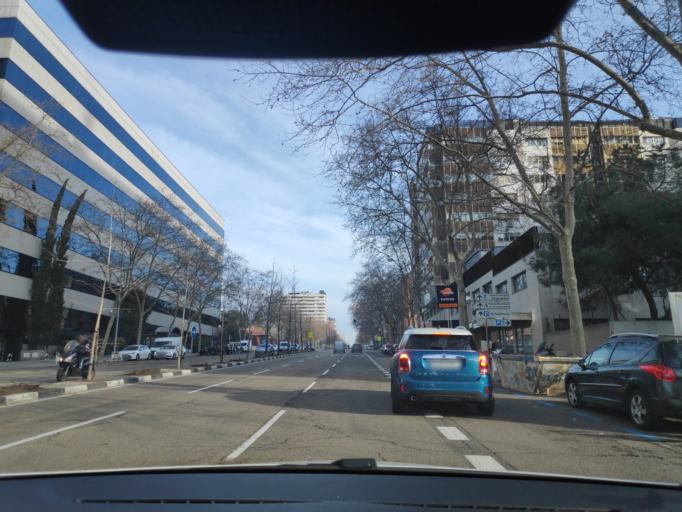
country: ES
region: Madrid
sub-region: Provincia de Madrid
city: Salamanca
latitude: 40.4432
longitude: -3.6783
